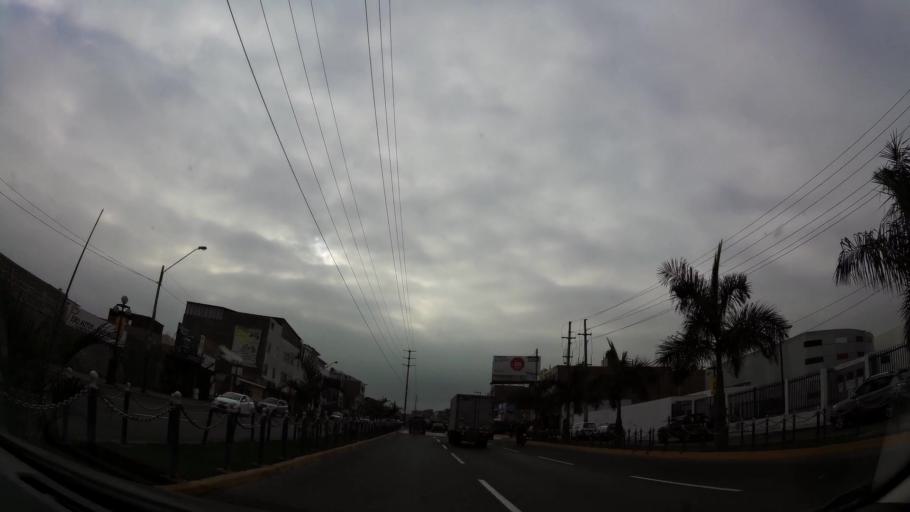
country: PE
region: Lima
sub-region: Lima
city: Surco
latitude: -12.1924
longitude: -77.0042
